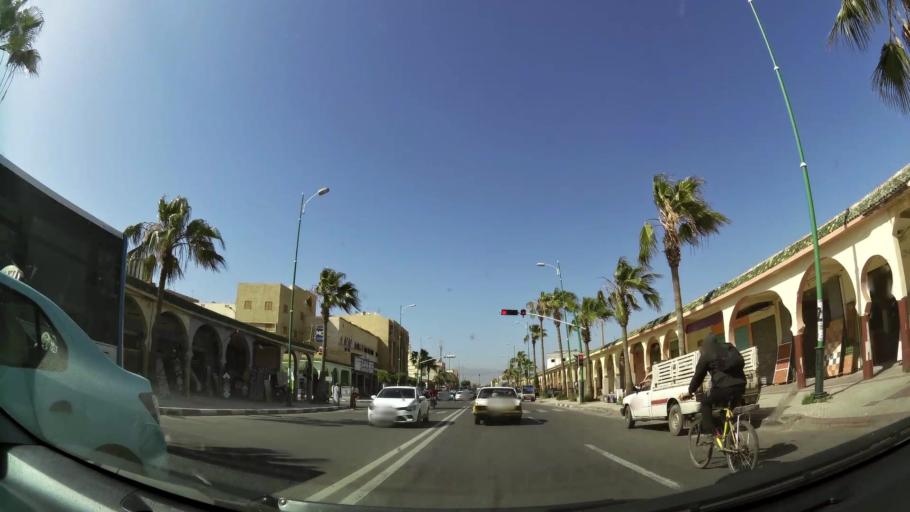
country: MA
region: Souss-Massa-Draa
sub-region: Inezgane-Ait Mellou
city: Inezgane
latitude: 30.3652
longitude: -9.5332
